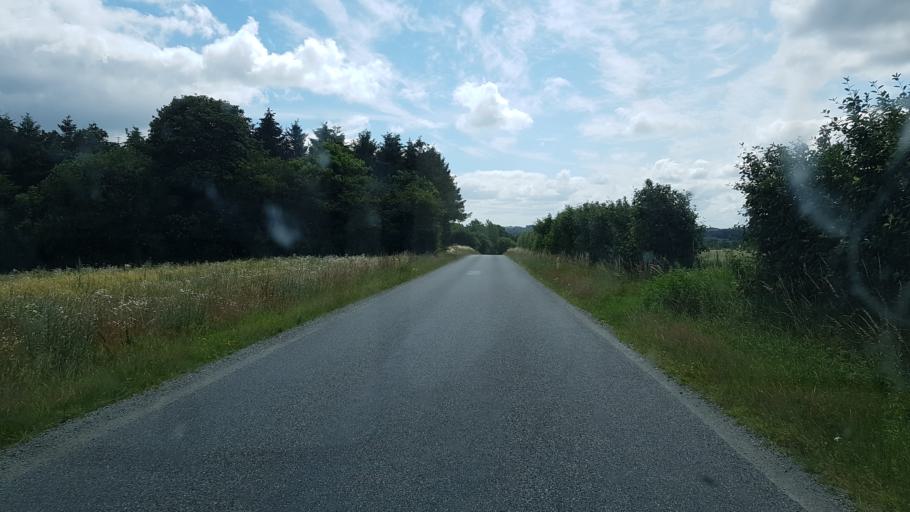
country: DK
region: South Denmark
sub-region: Vejen Kommune
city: Brorup
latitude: 55.4526
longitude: 8.9944
